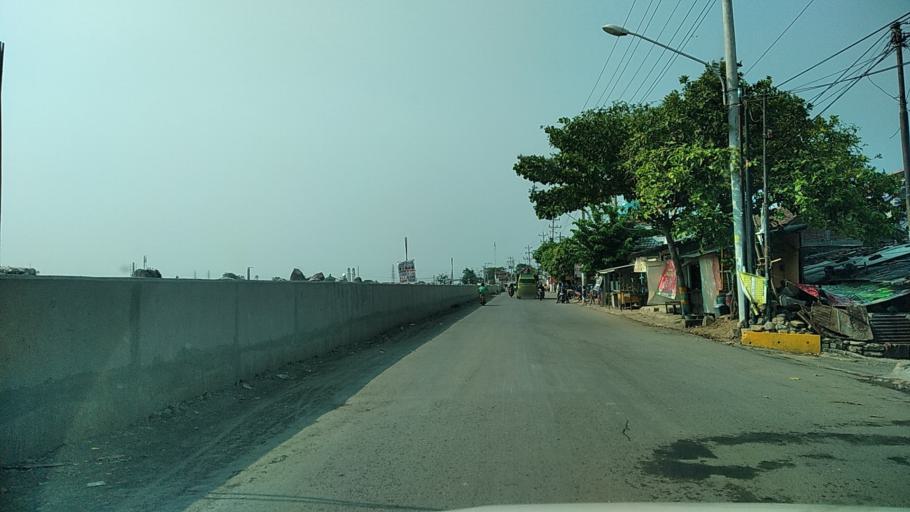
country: ID
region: Central Java
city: Semarang
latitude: -6.9630
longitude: 110.4441
